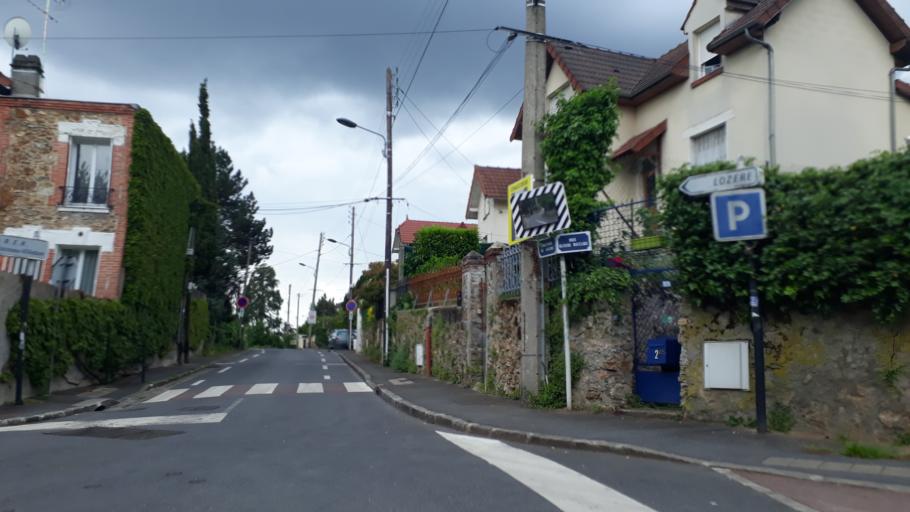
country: FR
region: Ile-de-France
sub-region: Departement de l'Essonne
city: Villebon-sur-Yvette
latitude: 48.7098
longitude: 2.2369
